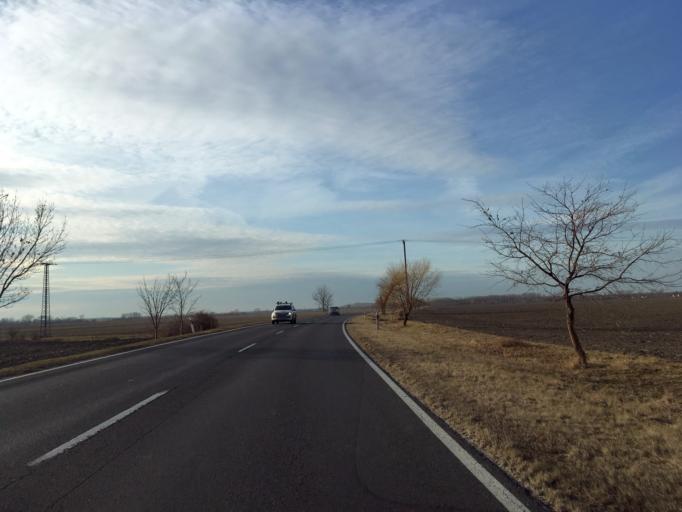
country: HU
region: Gyor-Moson-Sopron
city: Kimle
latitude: 47.8008
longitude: 17.3786
